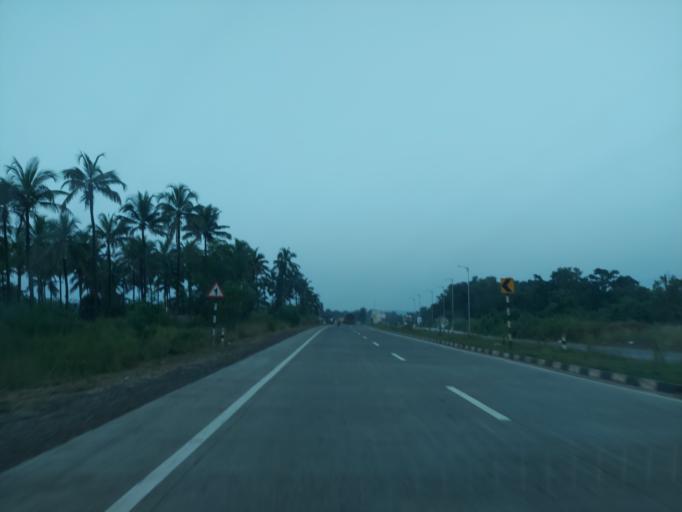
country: IN
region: Maharashtra
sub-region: Sindhudurg
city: Kudal
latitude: 16.1019
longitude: 73.7083
